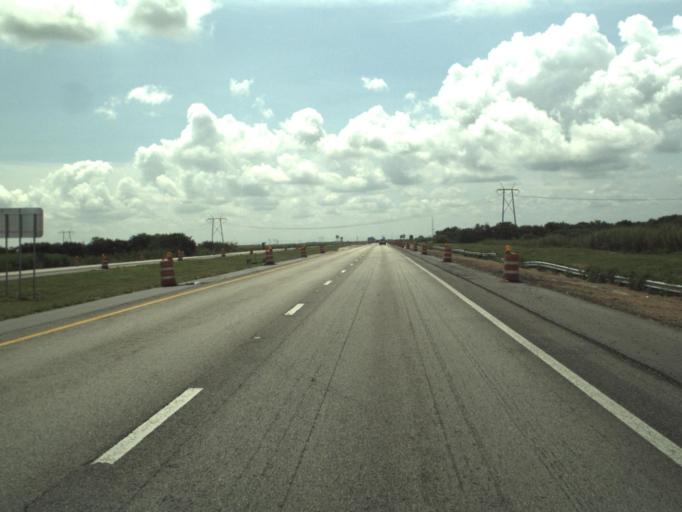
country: US
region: Florida
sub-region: Palm Beach County
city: Loxahatchee Groves
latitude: 26.7162
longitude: -80.4276
